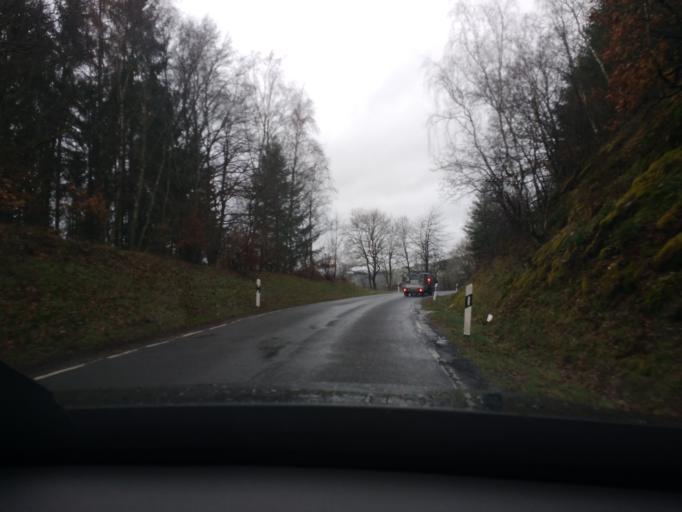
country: DE
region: Rheinland-Pfalz
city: Hinzenburg
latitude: 49.6686
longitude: 6.7260
